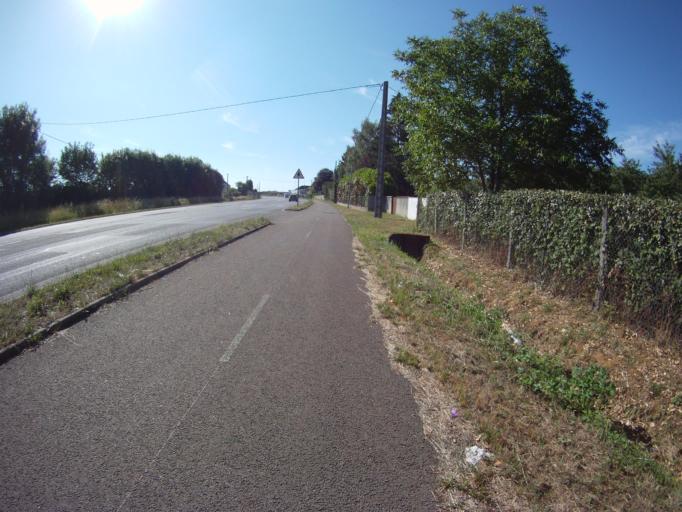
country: FR
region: Bourgogne
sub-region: Departement de la Nievre
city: Fourchambault
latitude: 47.0028
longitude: 3.0977
